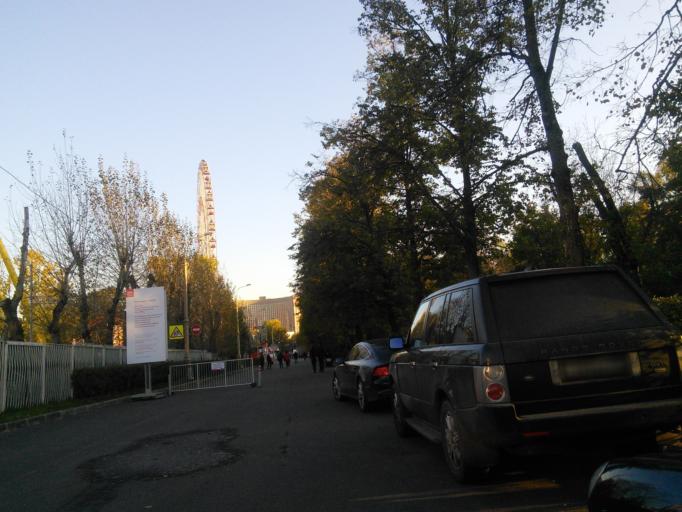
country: RU
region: Moscow
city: Sviblovo
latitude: 55.8297
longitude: 37.6380
